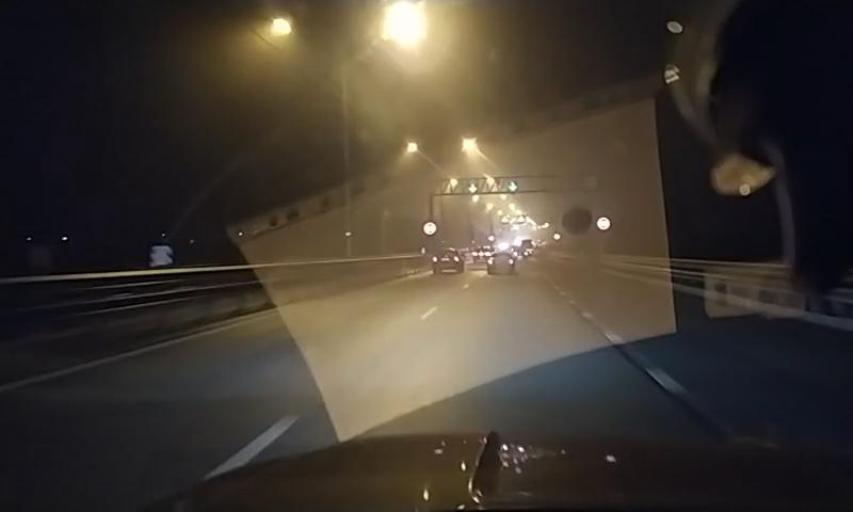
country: RU
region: Leningrad
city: Bugry
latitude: 60.1254
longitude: 30.3846
